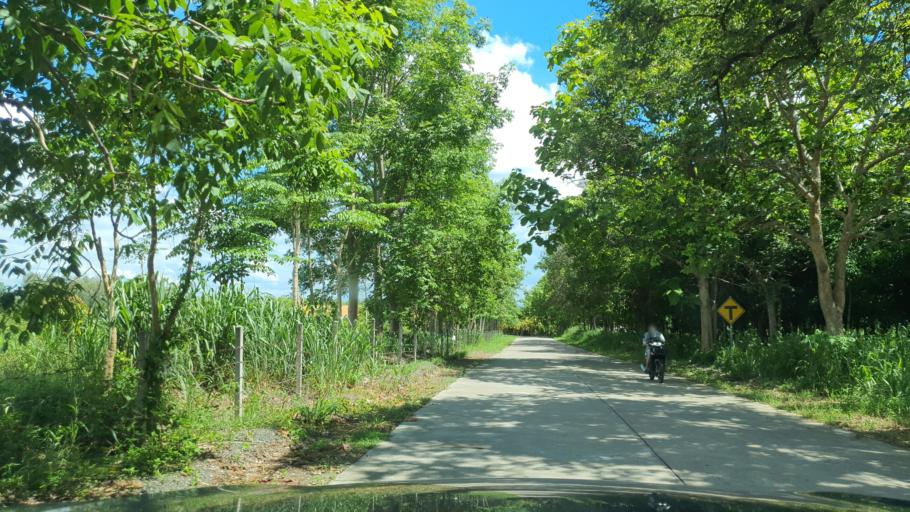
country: TH
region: Chiang Mai
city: San Sai
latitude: 18.9212
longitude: 99.0477
